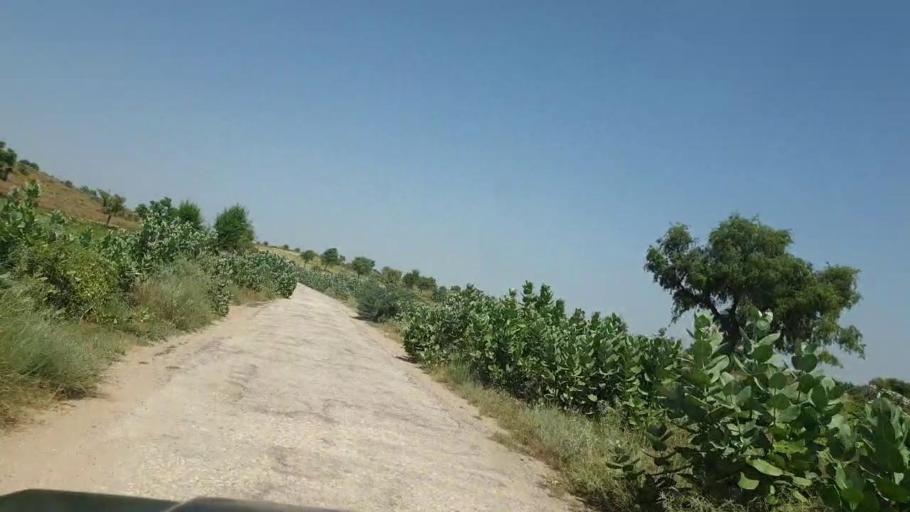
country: PK
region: Sindh
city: Chor
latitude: 25.3943
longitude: 70.3134
